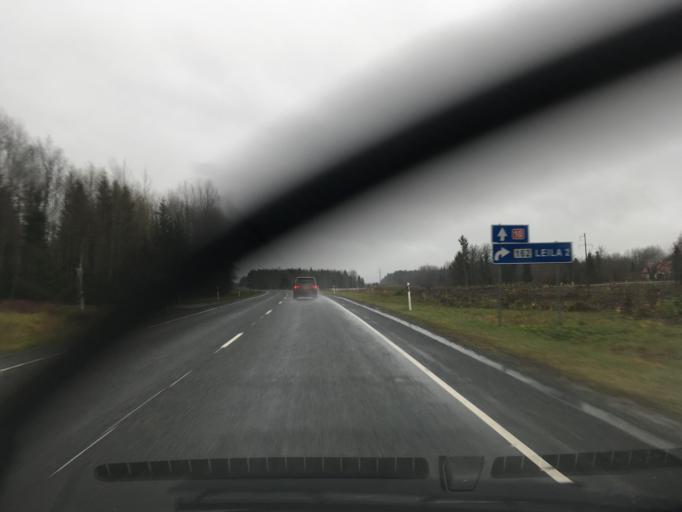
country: EE
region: Harju
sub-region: Nissi vald
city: Turba
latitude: 58.9410
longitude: 24.0885
